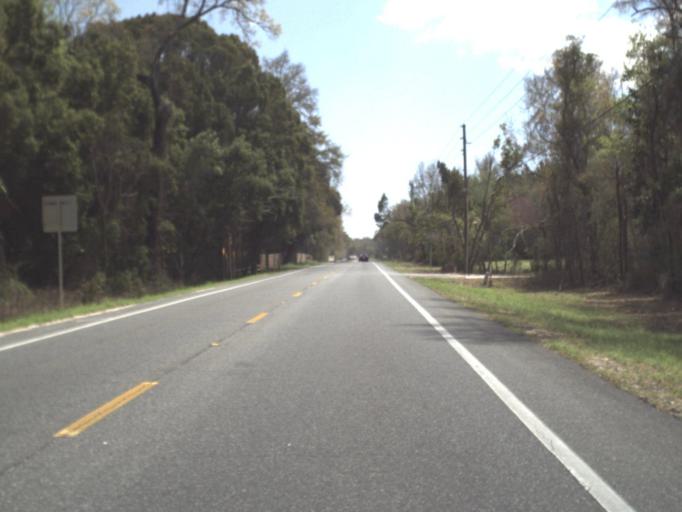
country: US
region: Florida
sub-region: Wakulla County
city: Crawfordville
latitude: 30.1144
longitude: -84.3828
